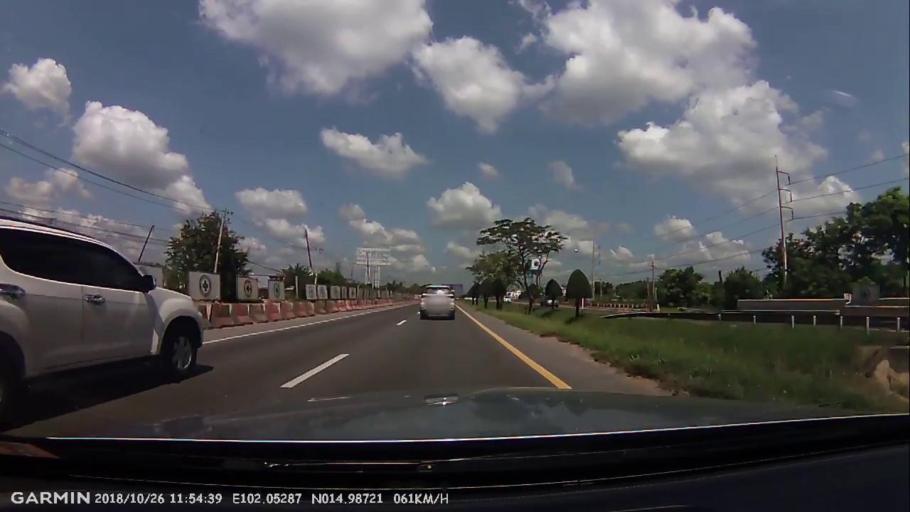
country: TH
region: Nakhon Ratchasima
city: Nakhon Ratchasima
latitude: 14.9874
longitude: 102.0529
